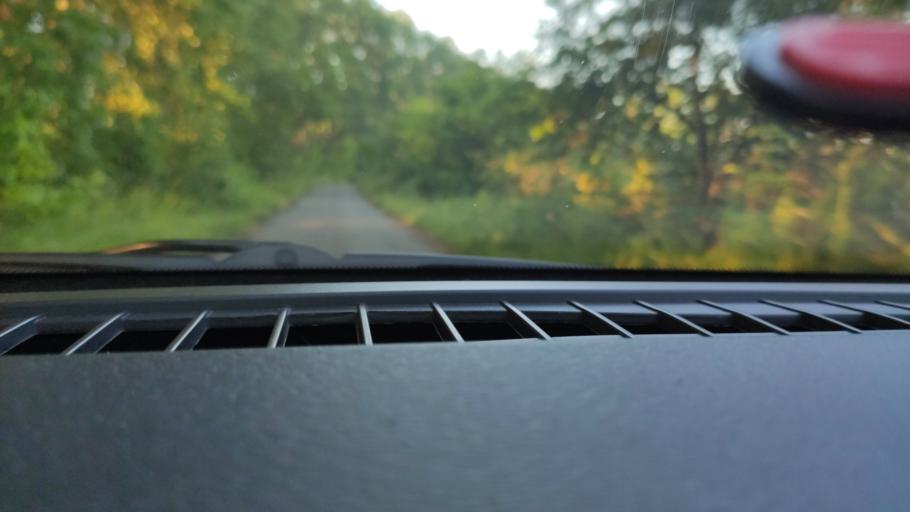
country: RU
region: Perm
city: Kondratovo
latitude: 57.9319
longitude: 56.0418
